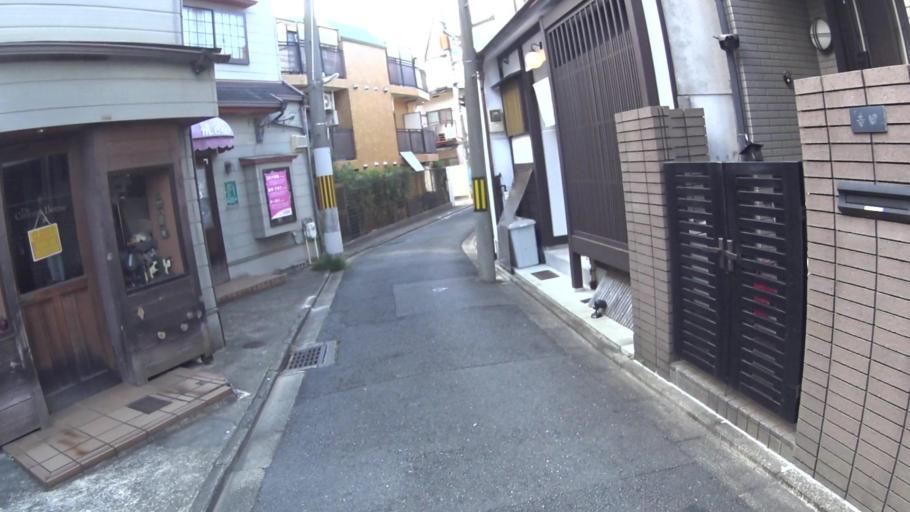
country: RU
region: Rostov
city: Remontnoye
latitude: 46.4991
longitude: 43.7769
